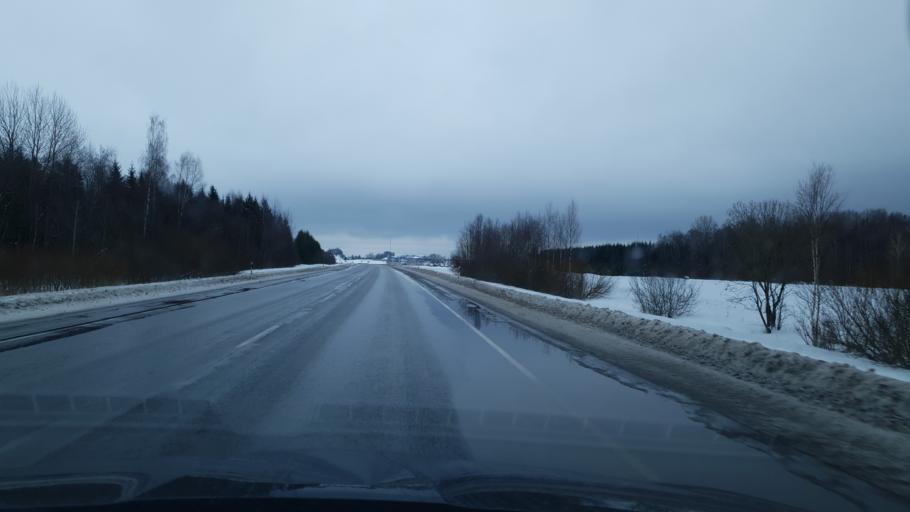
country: EE
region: Tartu
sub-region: Puhja vald
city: Puhja
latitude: 58.4829
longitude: 26.3421
